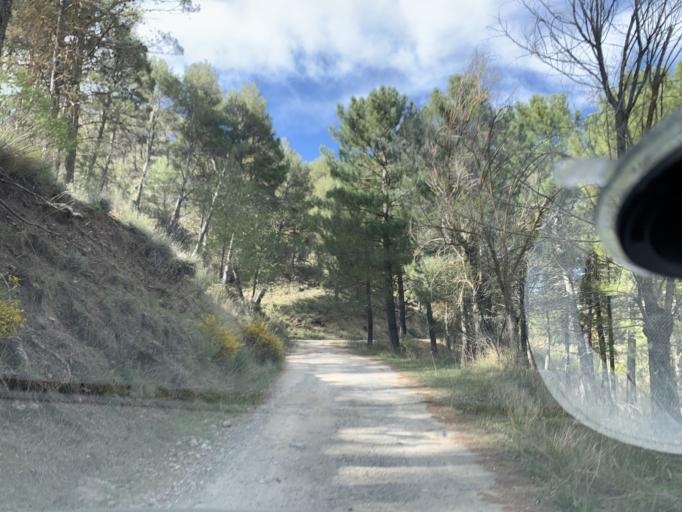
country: ES
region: Andalusia
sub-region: Provincia de Granada
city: Quentar
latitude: 37.2270
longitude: -3.4093
